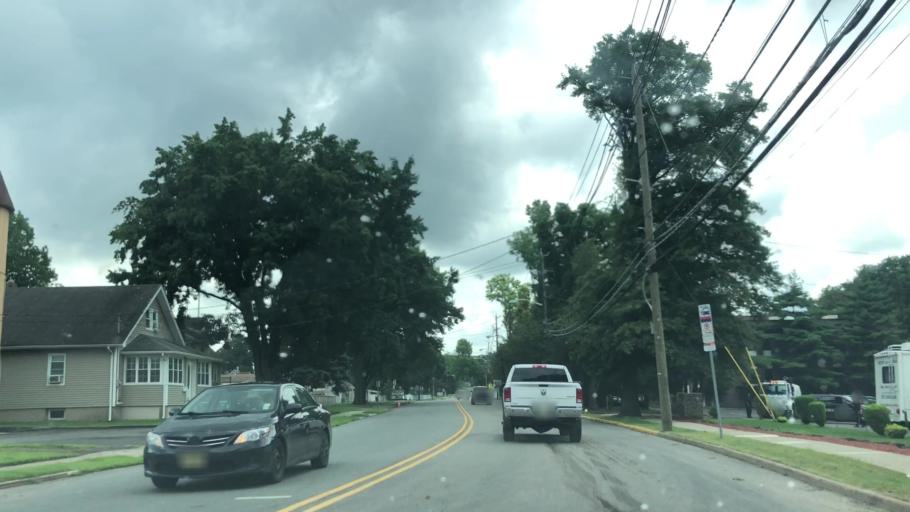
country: US
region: New Jersey
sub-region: Passaic County
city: Singac
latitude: 40.8877
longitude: -74.2210
